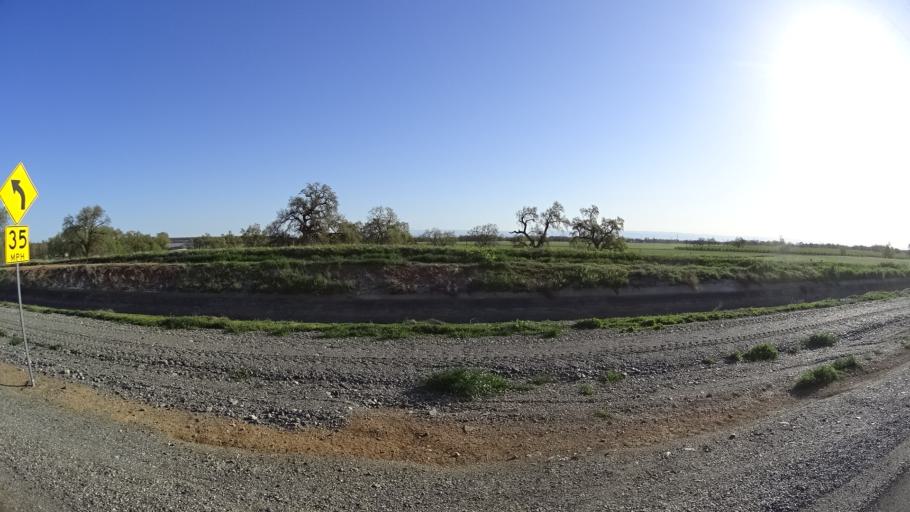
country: US
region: California
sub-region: Glenn County
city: Orland
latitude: 39.7863
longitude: -122.3012
